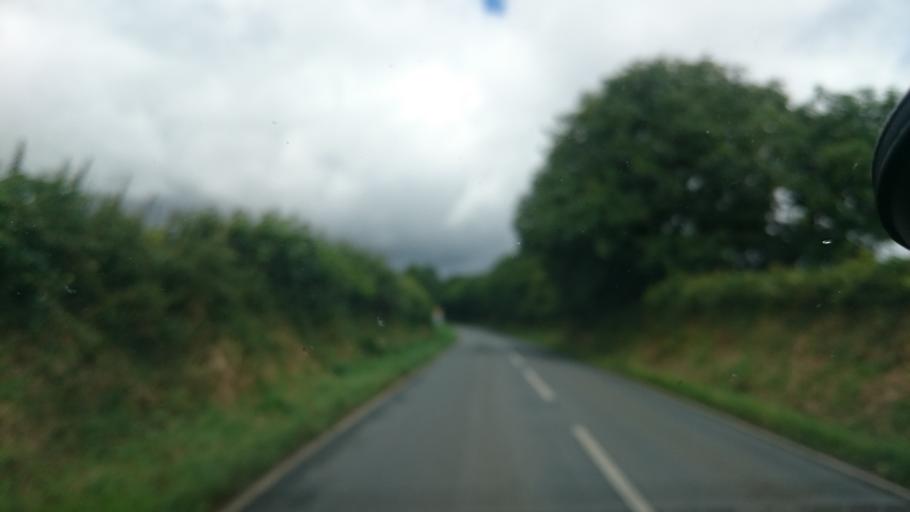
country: GB
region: Wales
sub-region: Pembrokeshire
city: Burton
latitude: 51.7325
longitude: -4.9212
